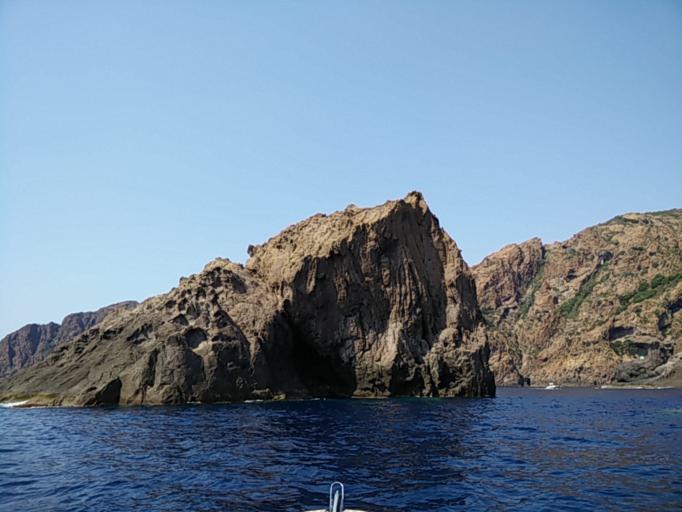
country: FR
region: Corsica
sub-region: Departement de la Corse-du-Sud
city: Cargese
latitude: 42.3562
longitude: 8.5531
